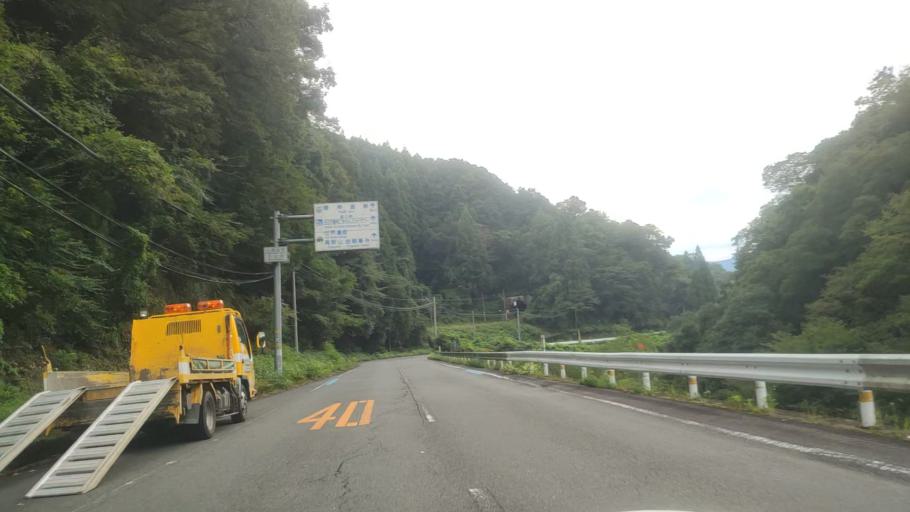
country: JP
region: Wakayama
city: Hashimoto
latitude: 34.2729
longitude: 135.5596
